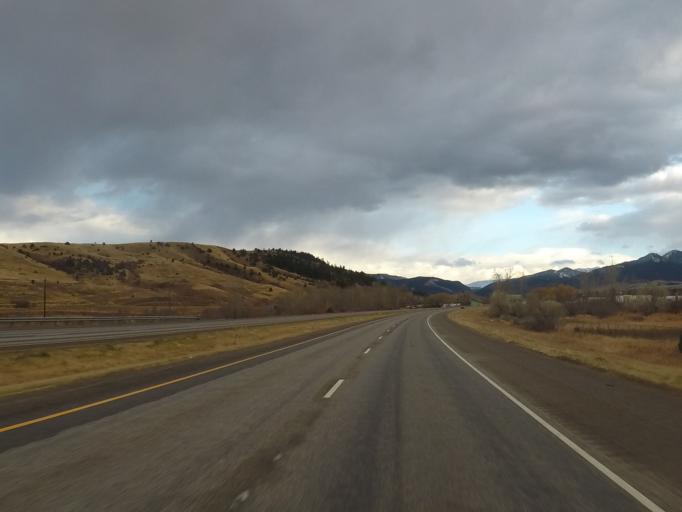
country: US
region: Montana
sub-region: Gallatin County
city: Bozeman
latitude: 45.6896
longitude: -111.0206
